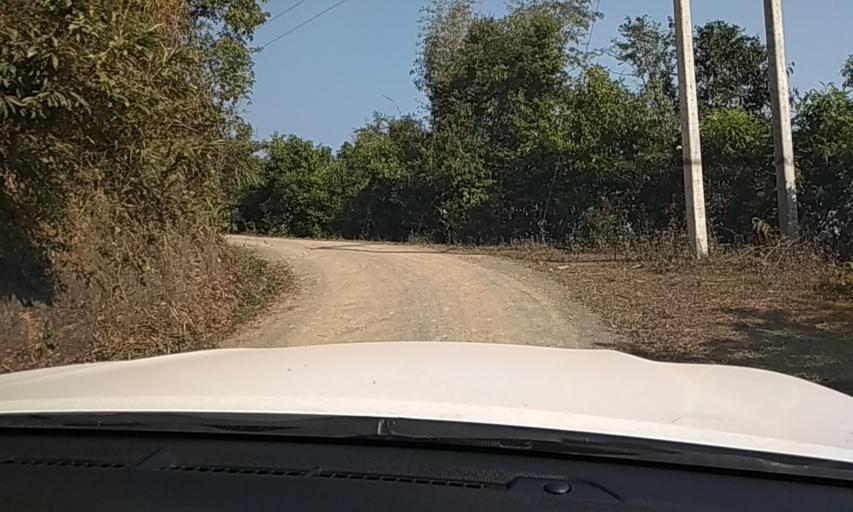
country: LA
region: Phongsali
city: Phongsali
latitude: 21.6966
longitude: 102.0833
